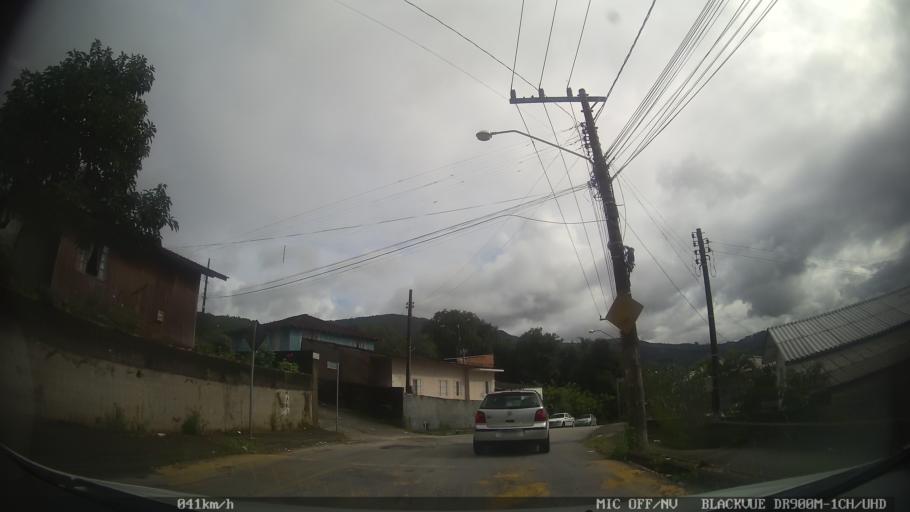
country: BR
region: Santa Catarina
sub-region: Biguacu
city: Biguacu
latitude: -27.5271
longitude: -48.6537
